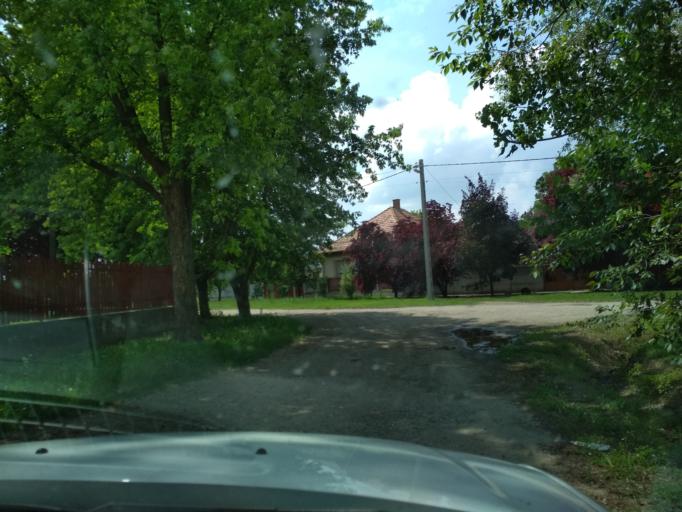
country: HU
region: Pest
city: Tapioszentmarton
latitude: 47.3352
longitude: 19.7506
